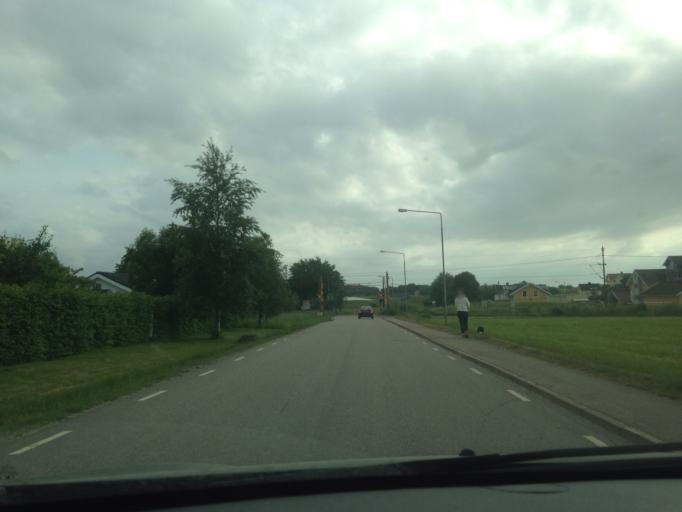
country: SE
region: Vaestra Goetaland
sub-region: Kungalvs Kommun
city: Kungalv
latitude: 57.8027
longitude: 11.9163
